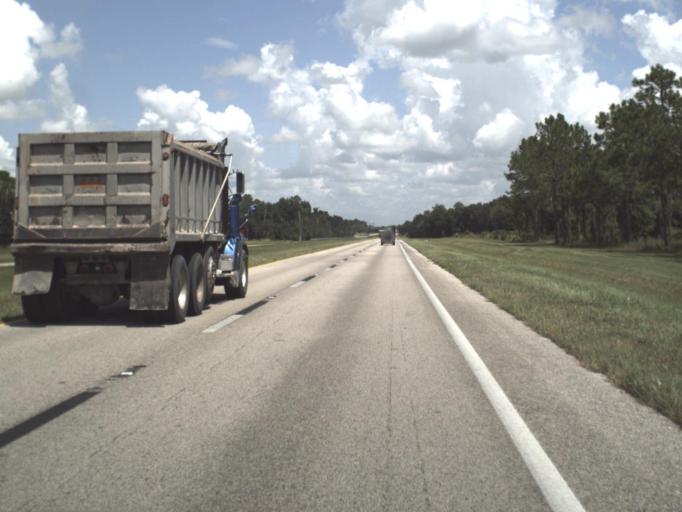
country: US
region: Florida
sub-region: Polk County
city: Fort Meade
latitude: 27.7001
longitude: -81.8098
